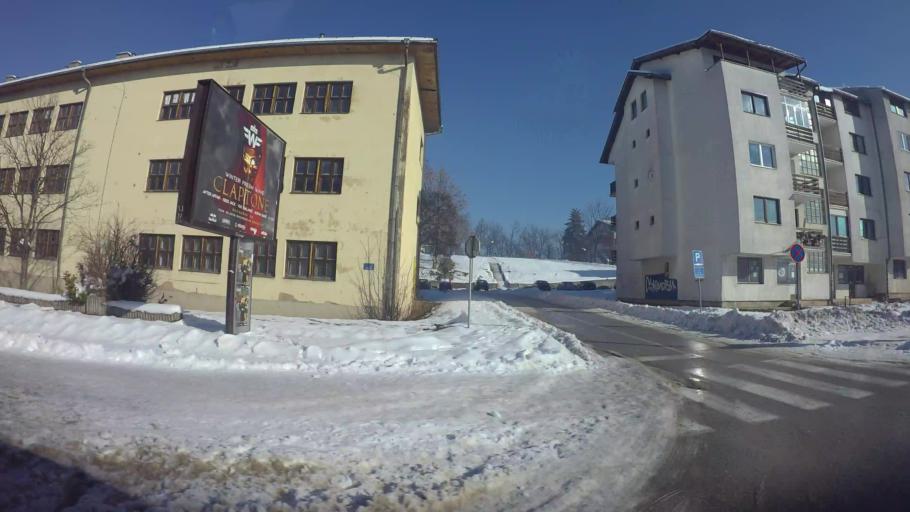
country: BA
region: Federation of Bosnia and Herzegovina
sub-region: Kanton Sarajevo
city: Sarajevo
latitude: 43.8231
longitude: 18.3661
